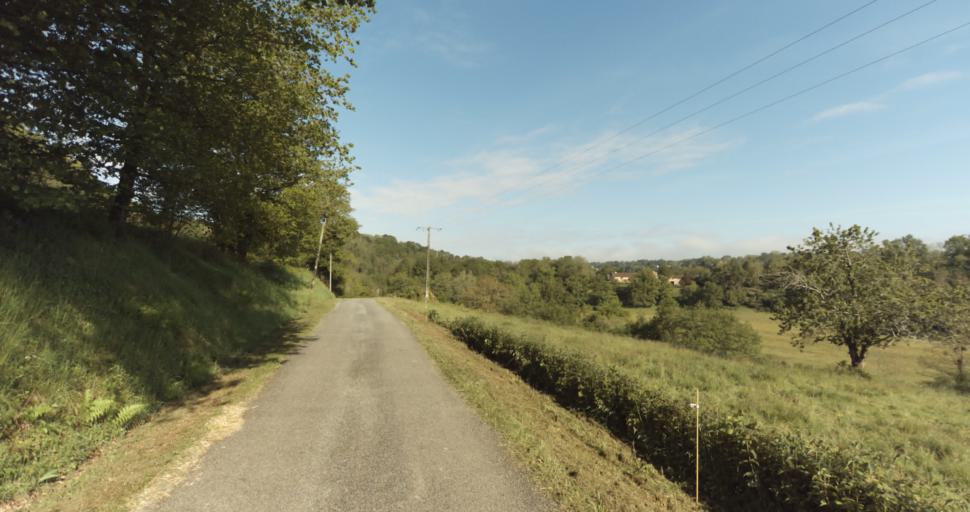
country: FR
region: Limousin
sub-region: Departement de la Haute-Vienne
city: Le Vigen
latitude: 45.7465
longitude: 1.2930
